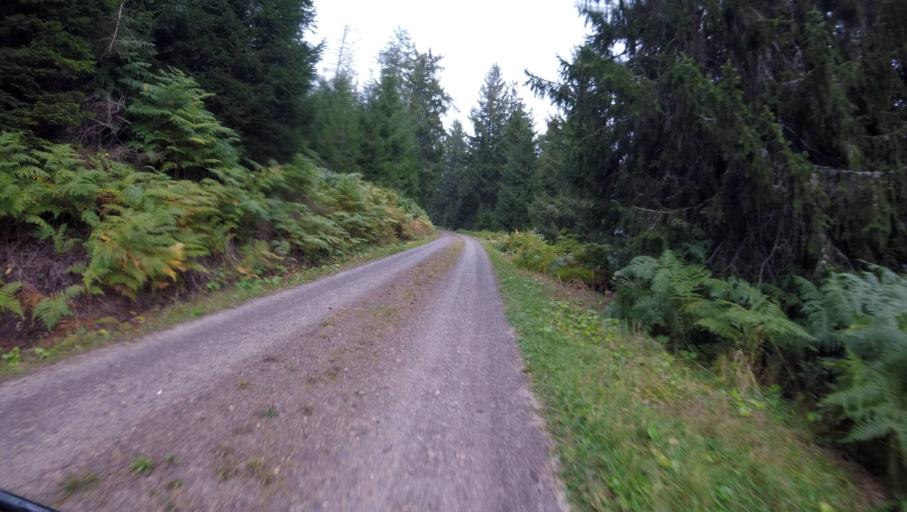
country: DE
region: Baden-Wuerttemberg
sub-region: Karlsruhe Region
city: Enzklosterle
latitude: 48.6736
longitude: 8.4194
